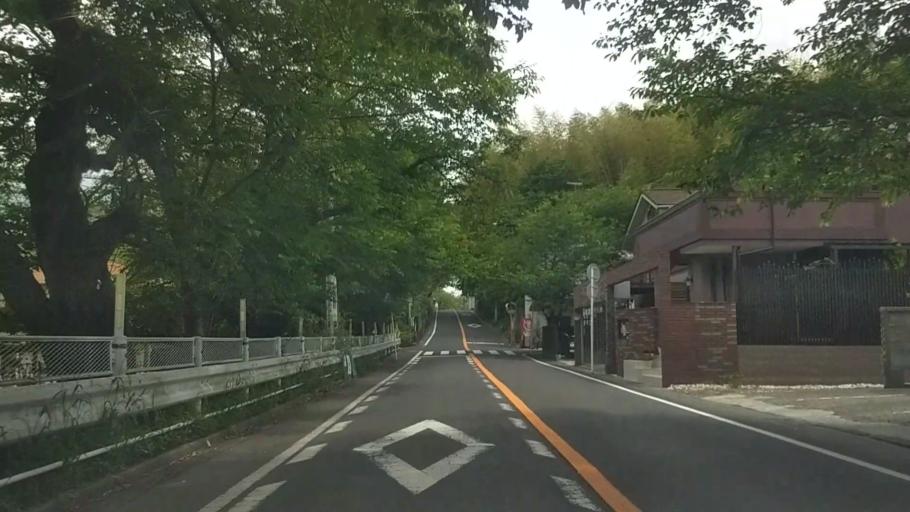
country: JP
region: Kanagawa
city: Kamakura
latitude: 35.3178
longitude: 139.5194
